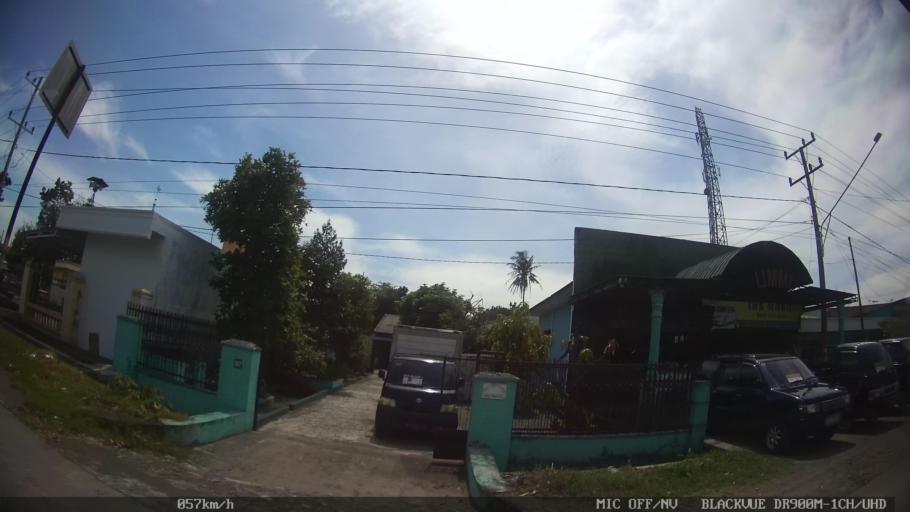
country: ID
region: North Sumatra
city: Binjai
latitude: 3.6367
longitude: 98.5107
